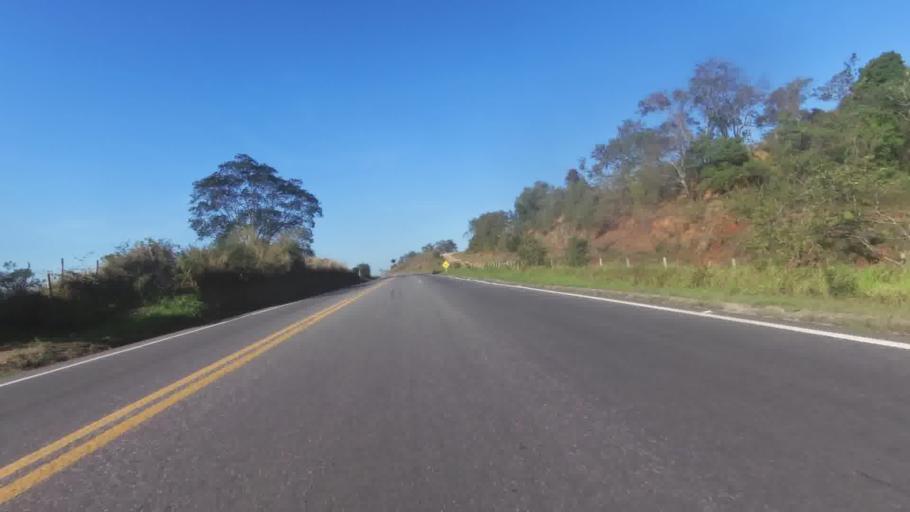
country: BR
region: Espirito Santo
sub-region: Alfredo Chaves
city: Alfredo Chaves
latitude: -20.6986
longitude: -40.7138
